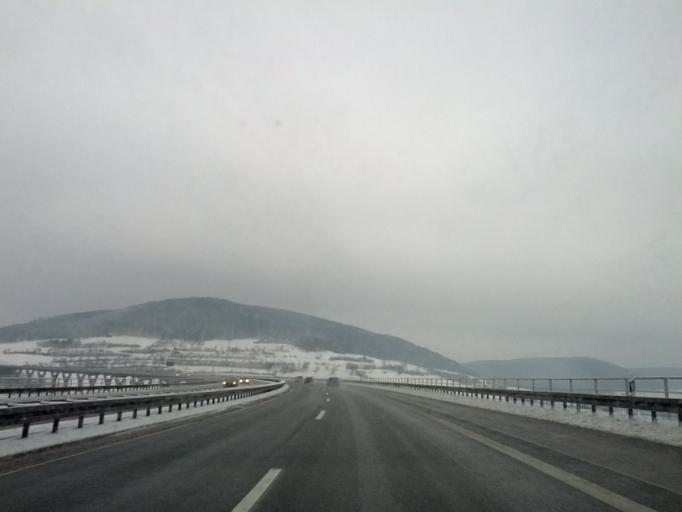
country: DE
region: Thuringia
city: Einhausen
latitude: 50.5243
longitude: 10.4735
